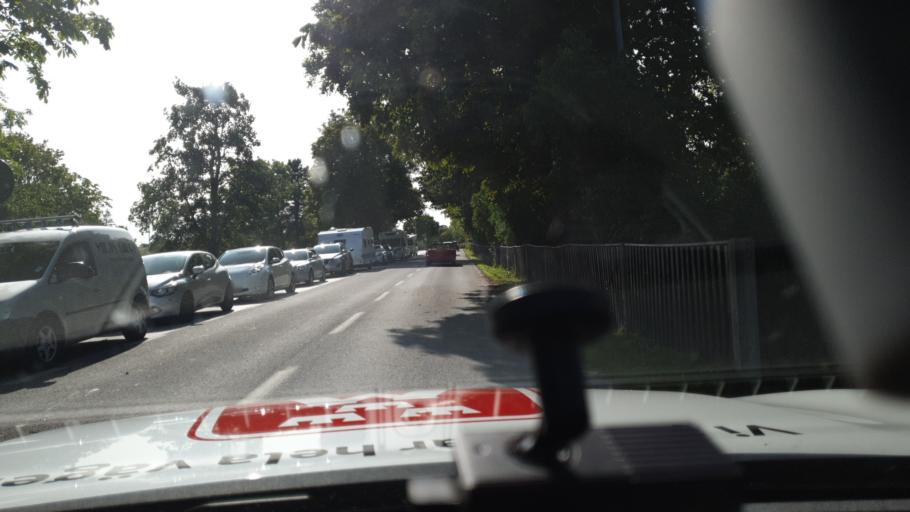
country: SE
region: Gotland
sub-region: Gotland
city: Slite
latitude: 57.8644
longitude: 19.0567
